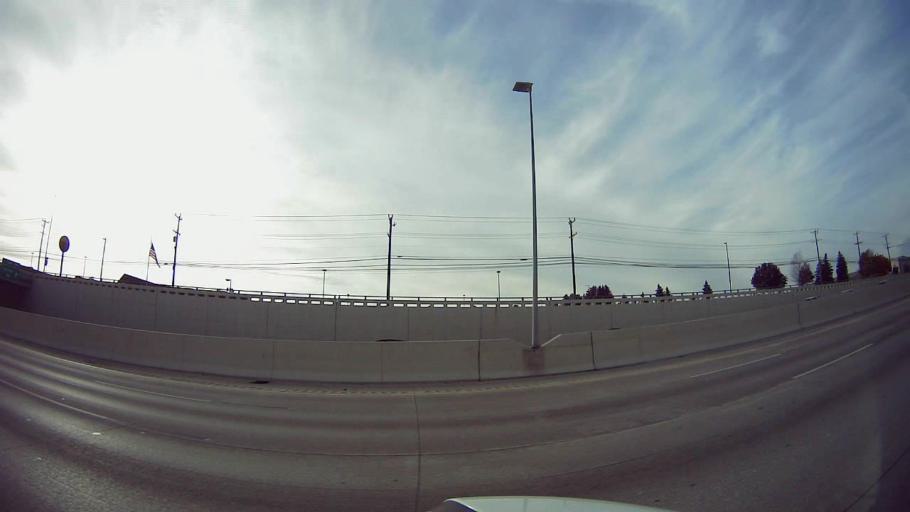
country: US
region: Michigan
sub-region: Wayne County
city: Redford
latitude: 42.3842
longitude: -83.3195
